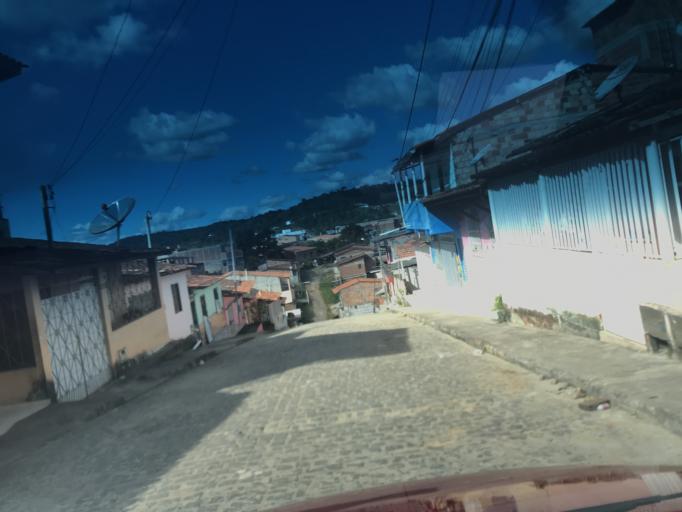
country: BR
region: Bahia
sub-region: Gandu
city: Gandu
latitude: -13.7468
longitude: -39.4929
